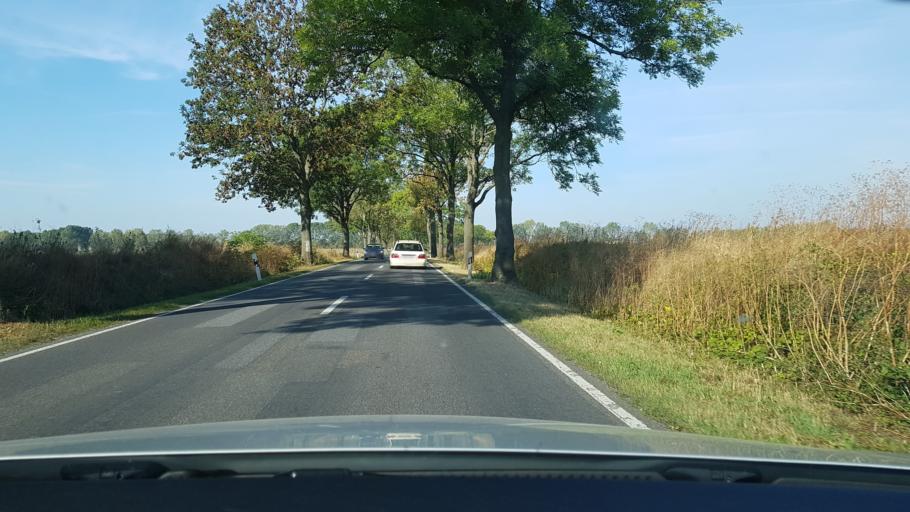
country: DE
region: Brandenburg
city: Beeskow
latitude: 52.1623
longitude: 14.2774
